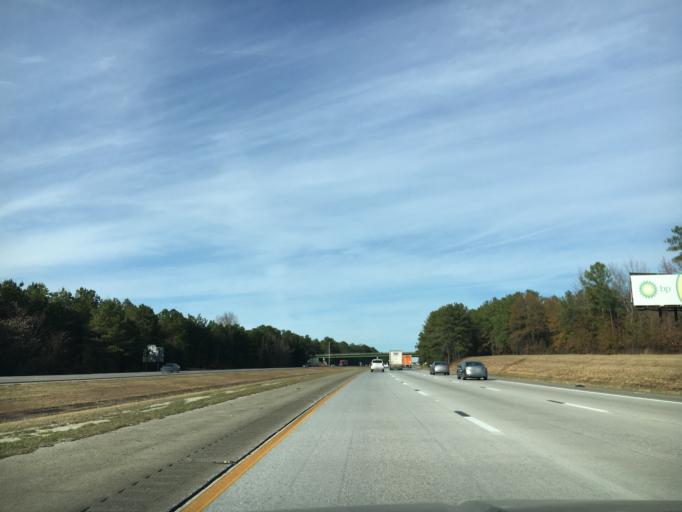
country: US
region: South Carolina
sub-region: Richland County
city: Blythewood
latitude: 34.1435
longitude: -80.9649
